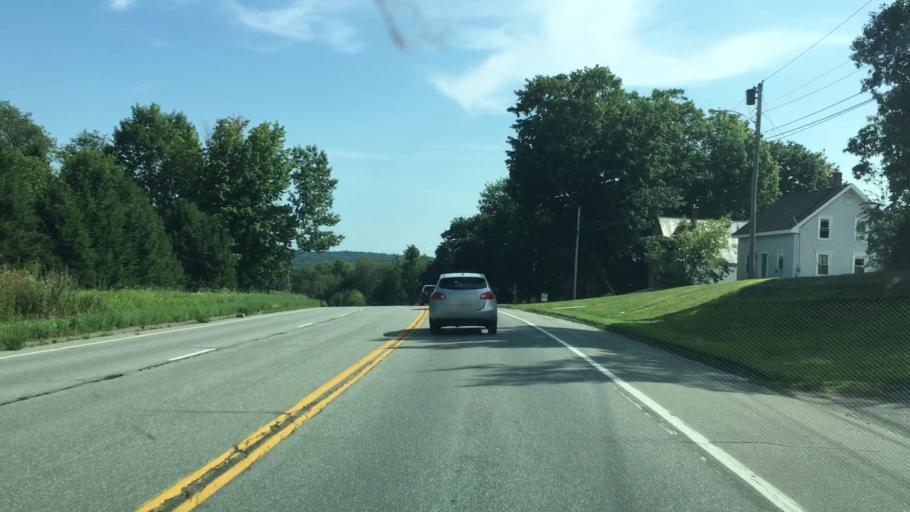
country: US
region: Maine
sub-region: Penobscot County
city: Orrington
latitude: 44.7080
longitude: -68.8470
